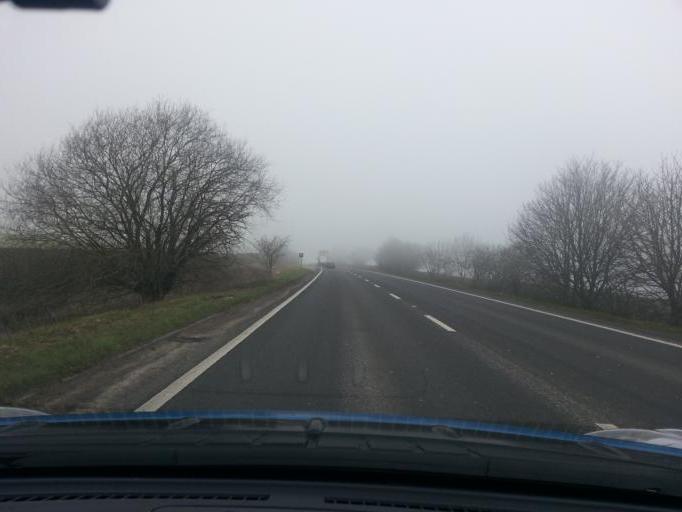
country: GB
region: England
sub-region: Oxfordshire
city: Faringdon
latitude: 51.6573
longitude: -1.5659
